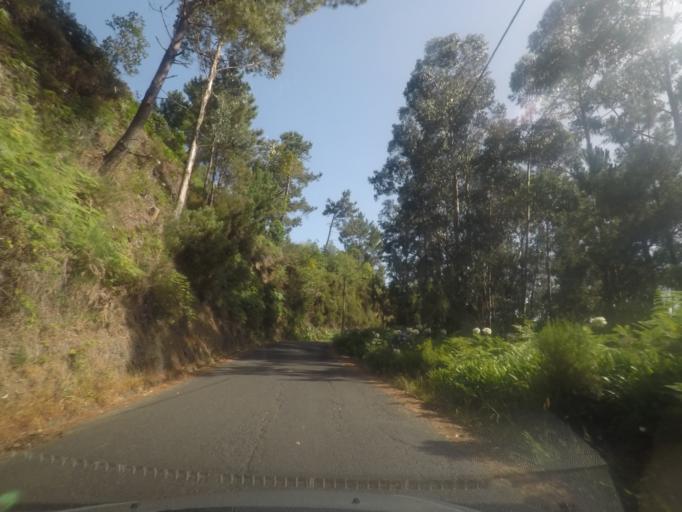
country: PT
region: Madeira
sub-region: Calheta
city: Estreito da Calheta
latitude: 32.7612
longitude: -17.2018
